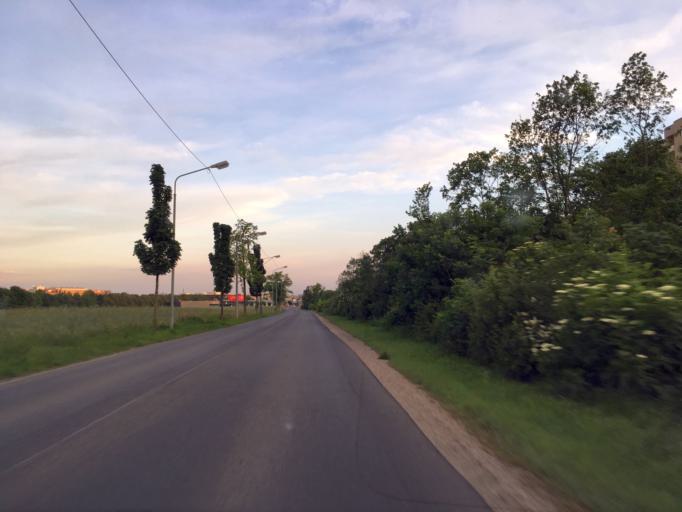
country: AT
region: Lower Austria
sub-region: Politischer Bezirk Wien-Umgebung
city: Gerasdorf bei Wien
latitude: 48.2721
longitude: 16.4568
